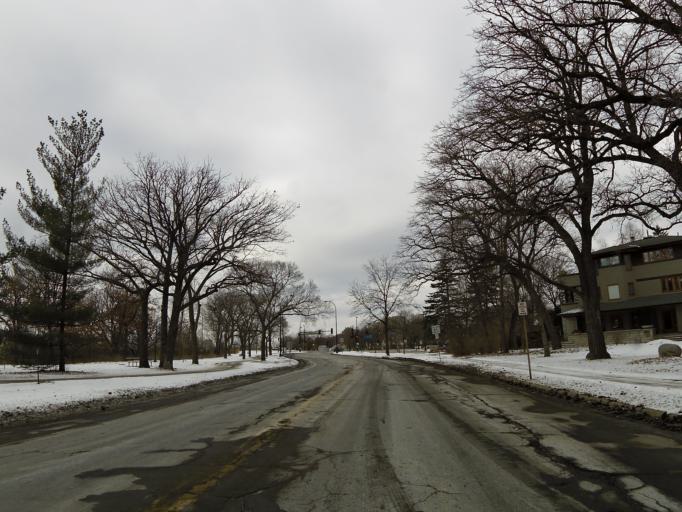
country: US
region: Minnesota
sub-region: Ramsey County
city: Lauderdale
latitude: 44.9638
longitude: -93.2194
